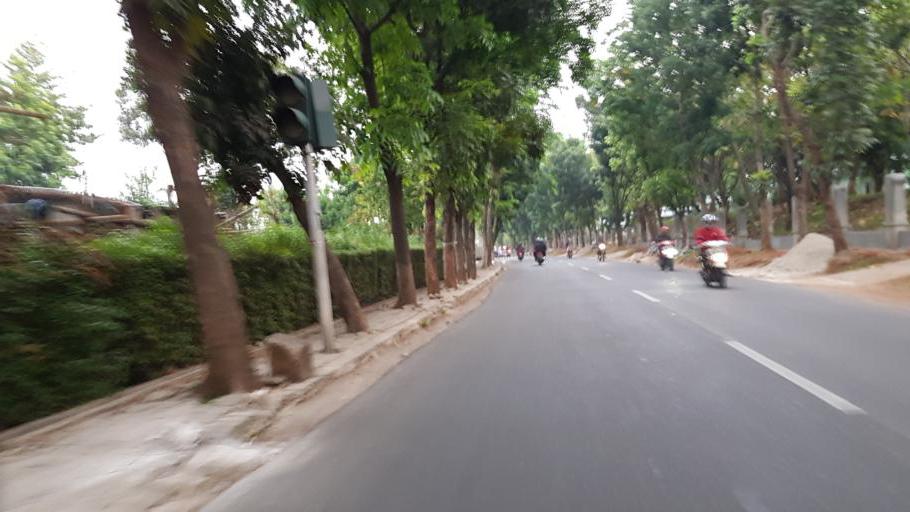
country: ID
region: West Java
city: Depok
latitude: -6.3262
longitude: 106.8449
